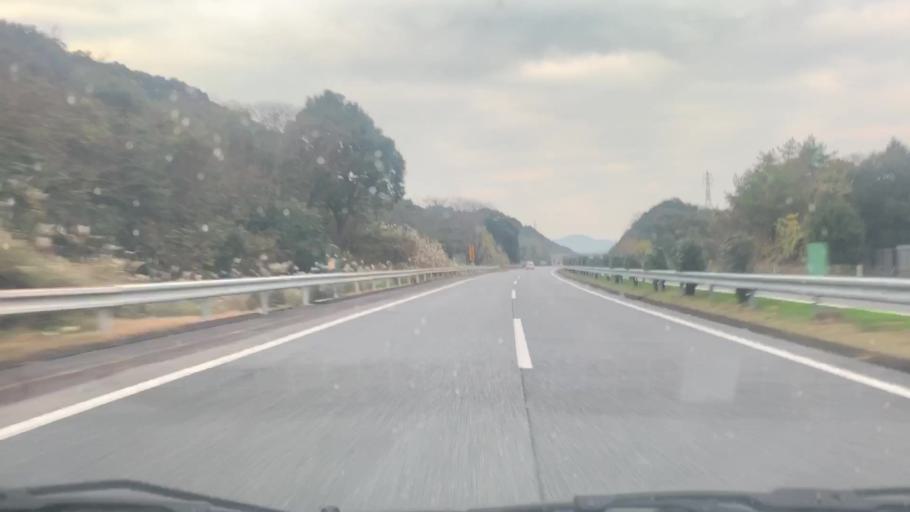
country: JP
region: Nagasaki
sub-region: Isahaya-shi
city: Isahaya
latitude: 32.8221
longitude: 129.9994
